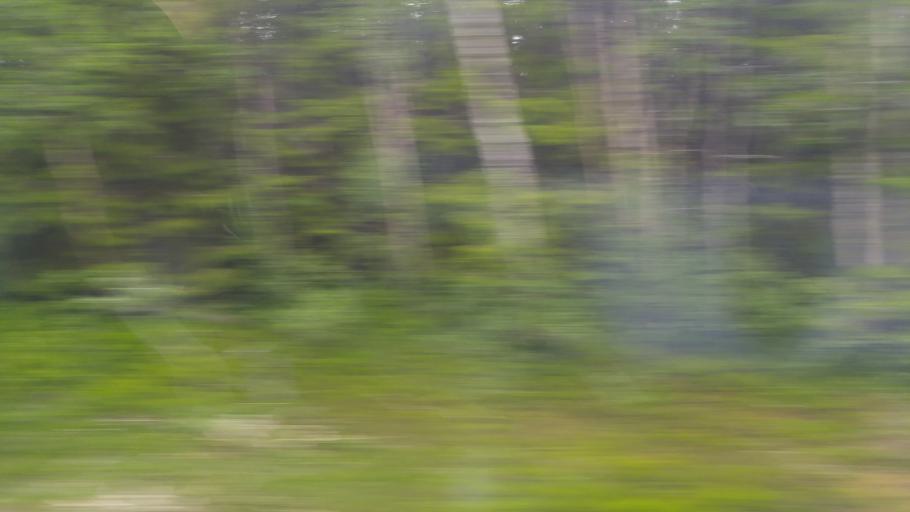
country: NO
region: Nord-Trondelag
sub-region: Meraker
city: Meraker
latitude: 63.3130
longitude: 12.2373
